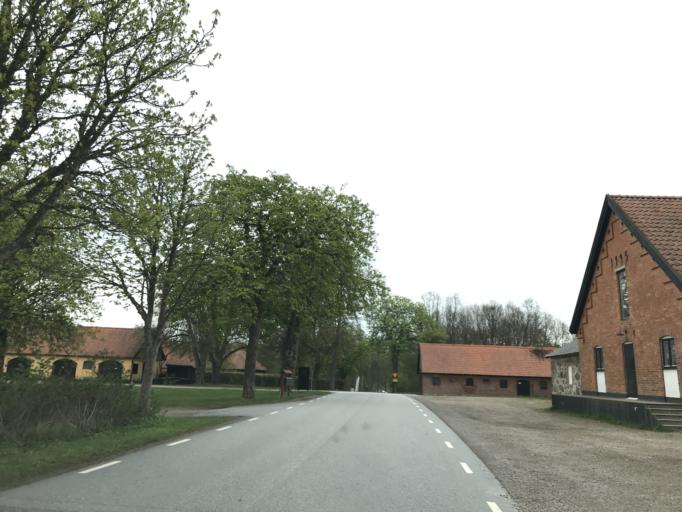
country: SE
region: Skane
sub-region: Trelleborgs Kommun
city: Anderslov
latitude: 55.5059
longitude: 13.3282
